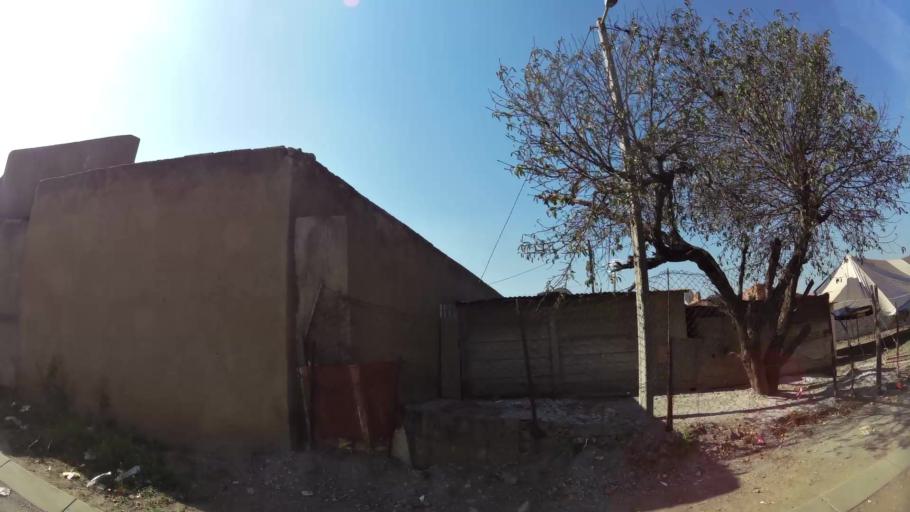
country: ZA
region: Gauteng
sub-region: Ekurhuleni Metropolitan Municipality
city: Boksburg
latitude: -26.2229
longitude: 28.2949
